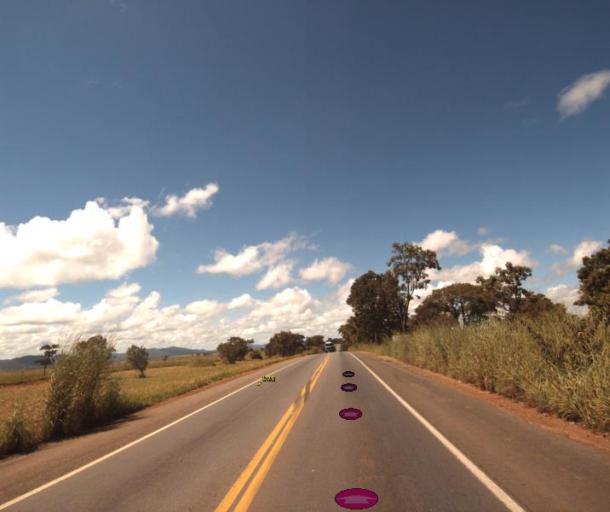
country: BR
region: Goias
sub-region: Jaragua
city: Jaragua
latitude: -15.8268
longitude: -49.2819
